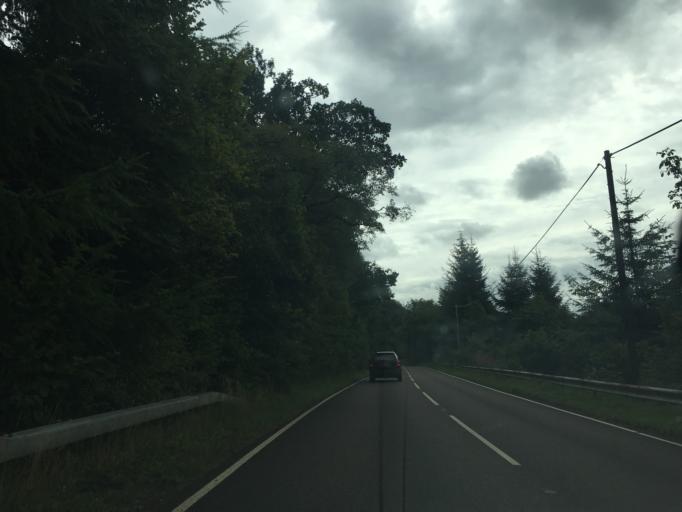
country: GB
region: Scotland
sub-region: Stirling
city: Callander
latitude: 56.2909
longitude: -4.2856
